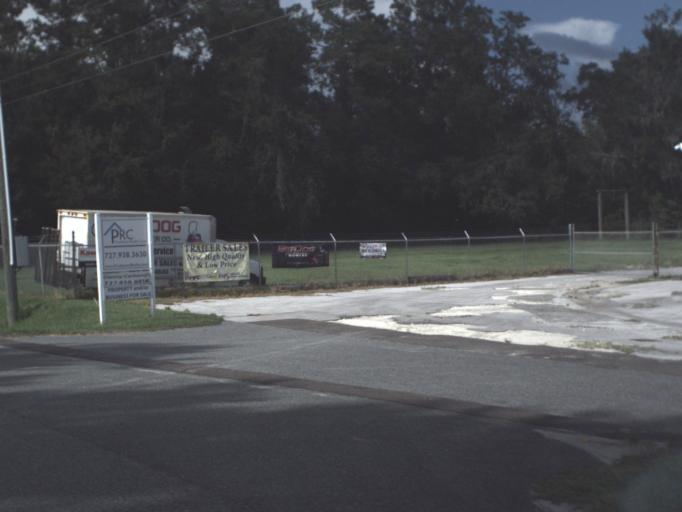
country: US
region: Florida
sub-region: Hernando County
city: Brooksville
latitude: 28.5642
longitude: -82.3976
